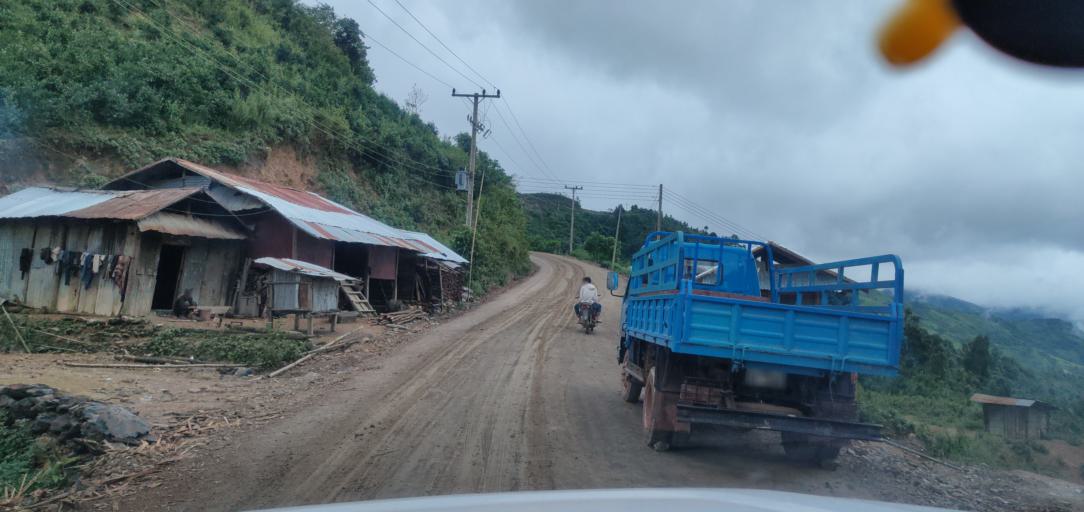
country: LA
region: Phongsali
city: Phongsali
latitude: 21.4285
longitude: 102.1672
